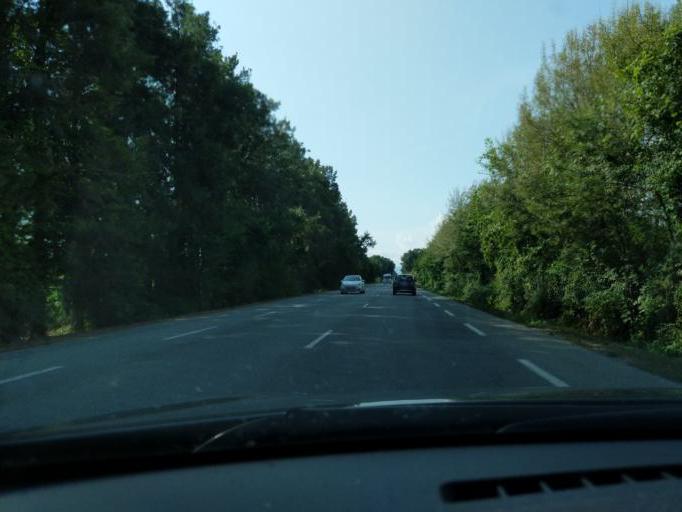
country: FR
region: Corsica
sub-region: Departement de la Haute-Corse
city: Ghisonaccia
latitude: 41.9704
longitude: 9.3985
